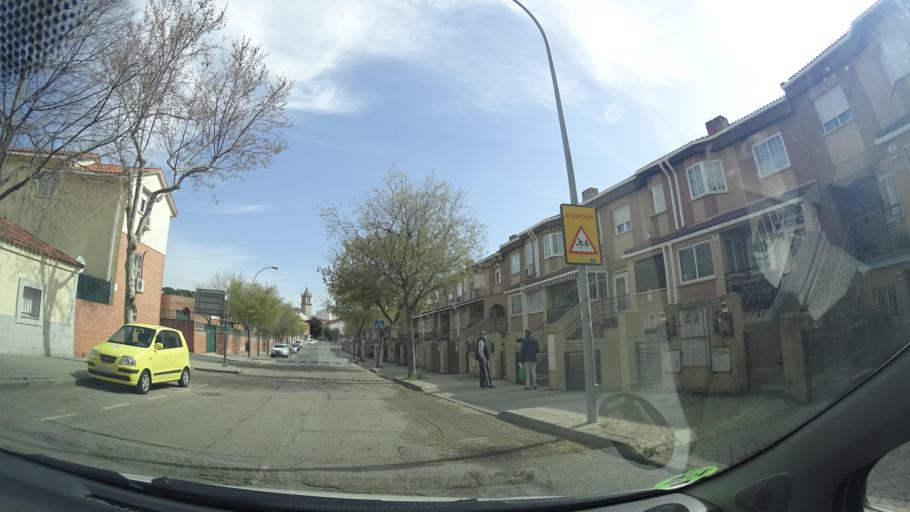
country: ES
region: Madrid
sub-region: Provincia de Madrid
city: Colmenar Viejo
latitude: 40.6541
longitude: -3.7704
